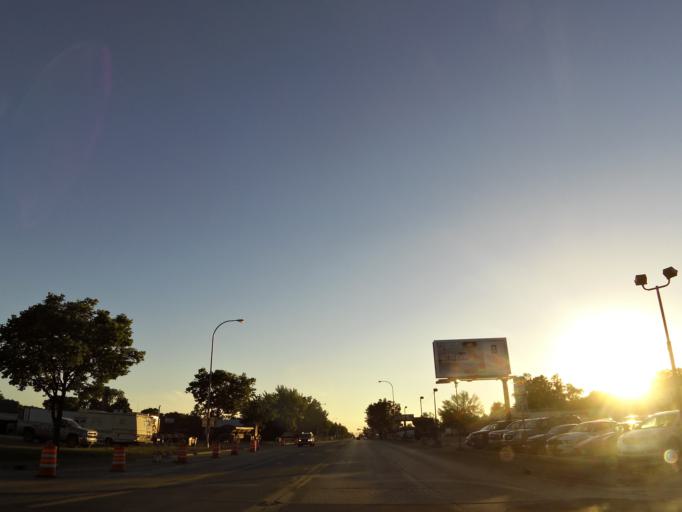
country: US
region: North Dakota
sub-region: Grand Forks County
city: Grand Forks
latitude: 47.9332
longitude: -97.0411
